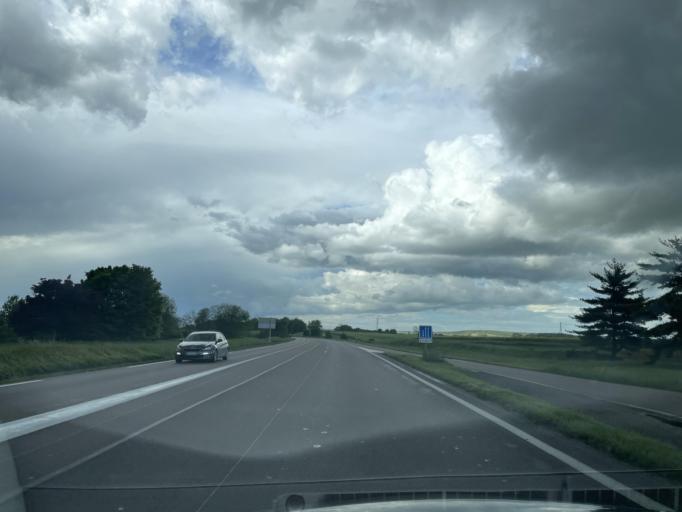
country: FR
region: Bourgogne
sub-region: Departement de l'Yonne
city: Saint-Clement
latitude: 48.2096
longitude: 3.3108
